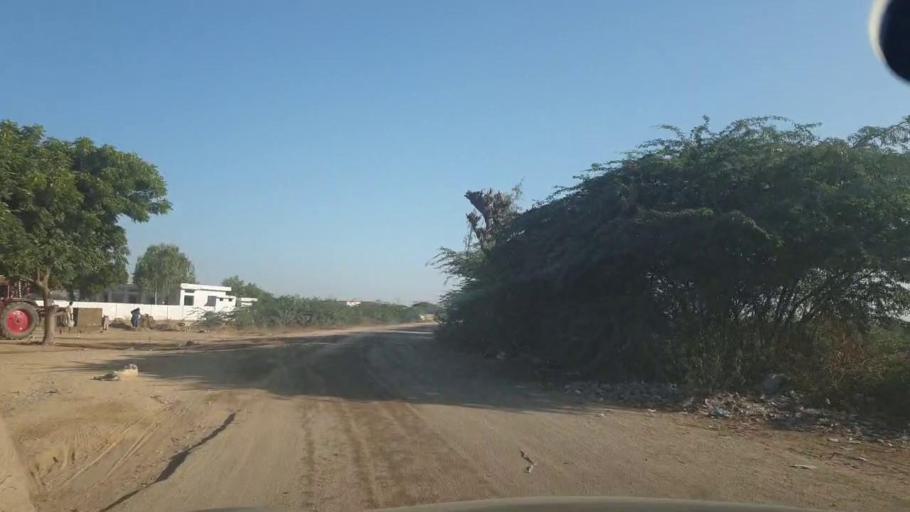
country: PK
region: Sindh
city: Malir Cantonment
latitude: 25.1110
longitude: 67.2669
